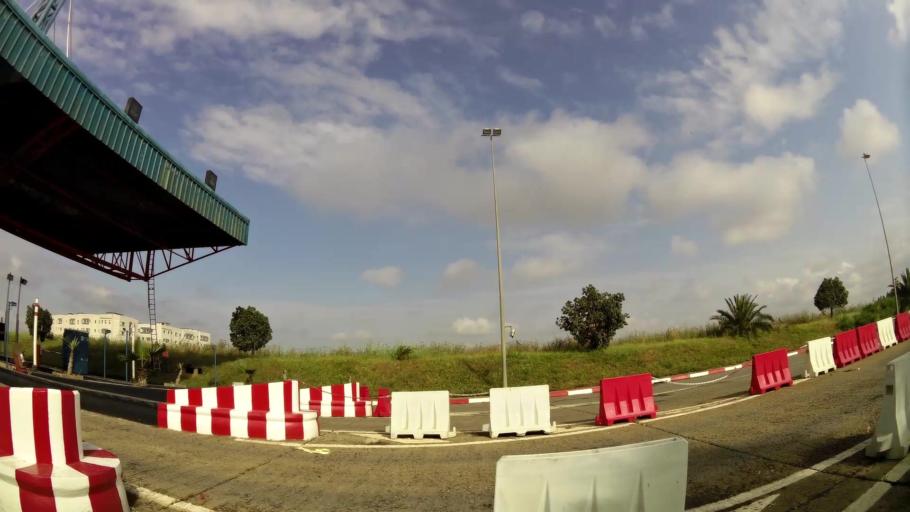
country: MA
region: Rabat-Sale-Zemmour-Zaer
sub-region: Khemisset
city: Tiflet
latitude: 33.8815
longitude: -6.3222
